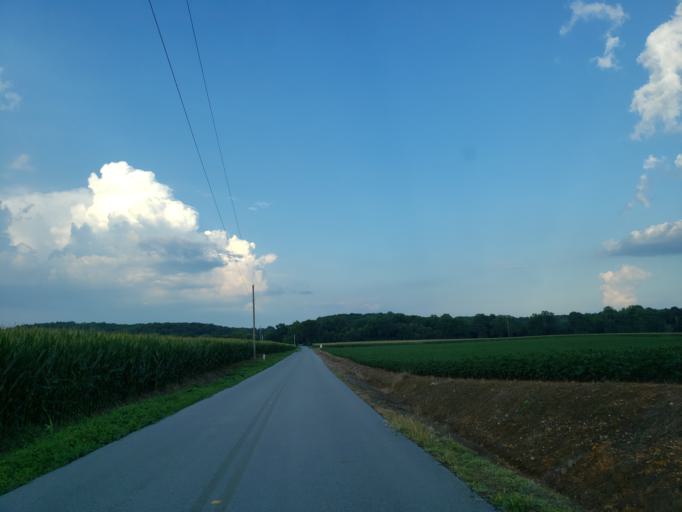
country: US
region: Georgia
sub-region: Bartow County
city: Euharlee
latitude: 34.0753
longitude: -84.9573
